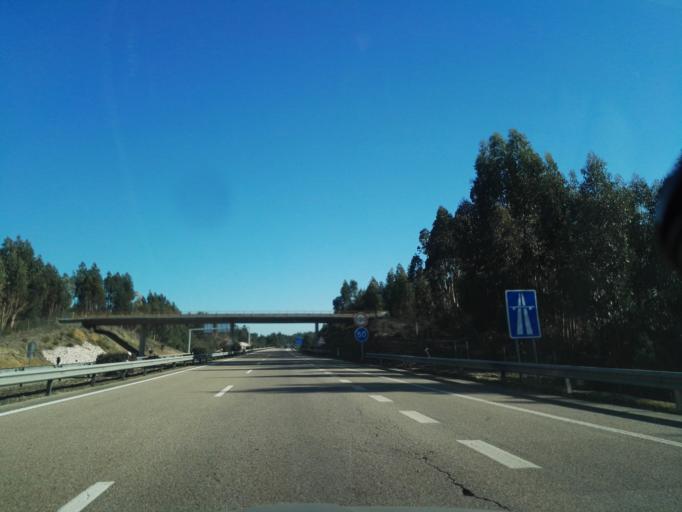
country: PT
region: Santarem
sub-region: Constancia
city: Constancia
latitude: 39.4866
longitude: -8.3874
